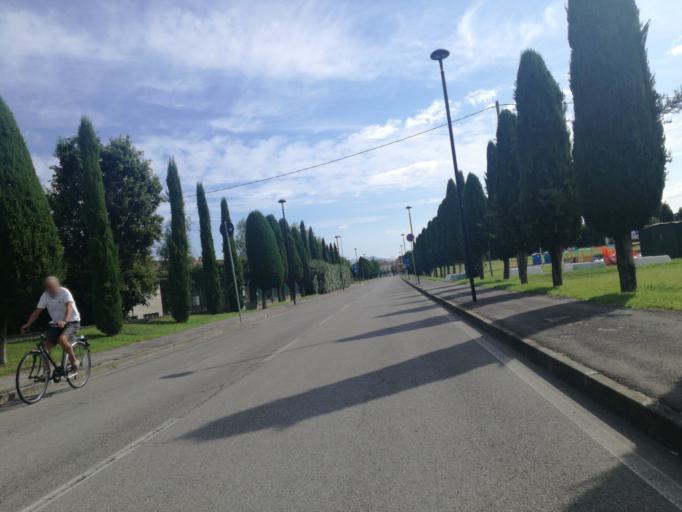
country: IT
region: Lombardy
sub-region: Provincia di Bergamo
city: Calusco d'Adda
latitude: 45.6876
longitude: 9.4631
